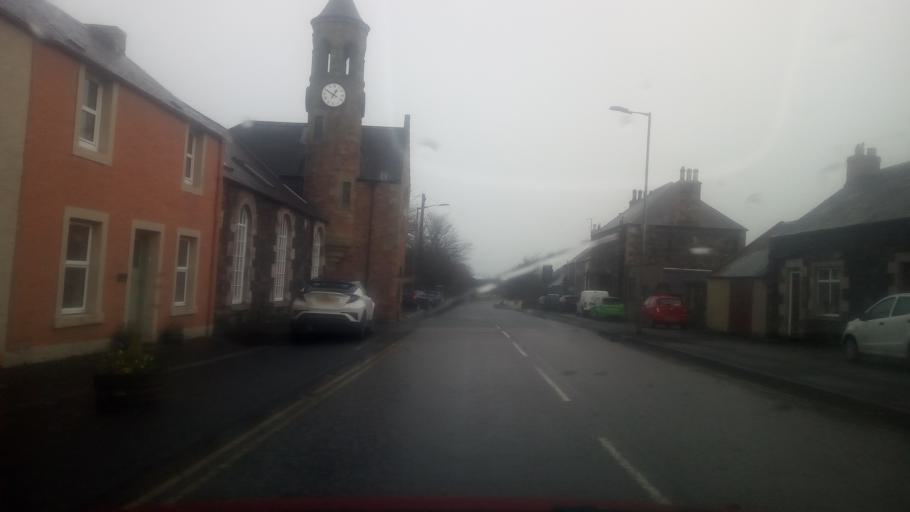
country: GB
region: Scotland
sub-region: The Scottish Borders
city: Earlston
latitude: 55.6802
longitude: -2.5619
